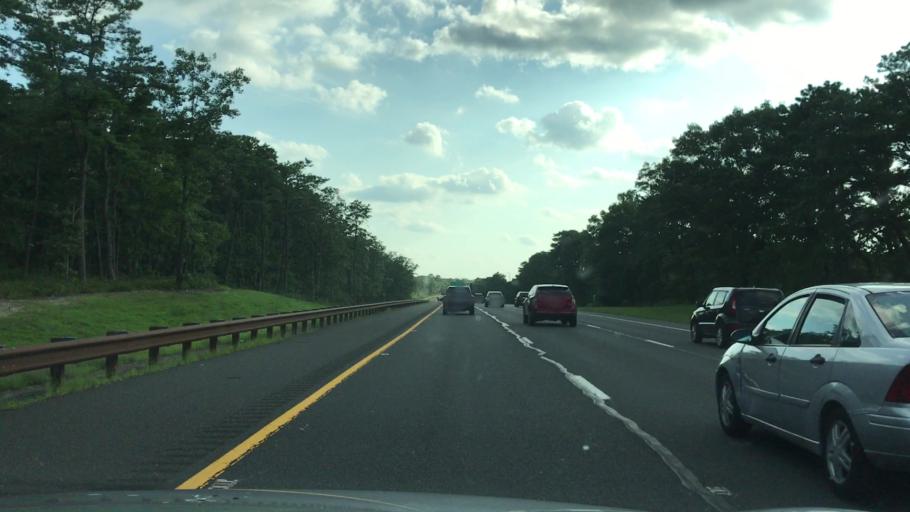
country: US
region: New Jersey
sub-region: Ocean County
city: Tuckerton
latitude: 39.6611
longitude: -74.3282
